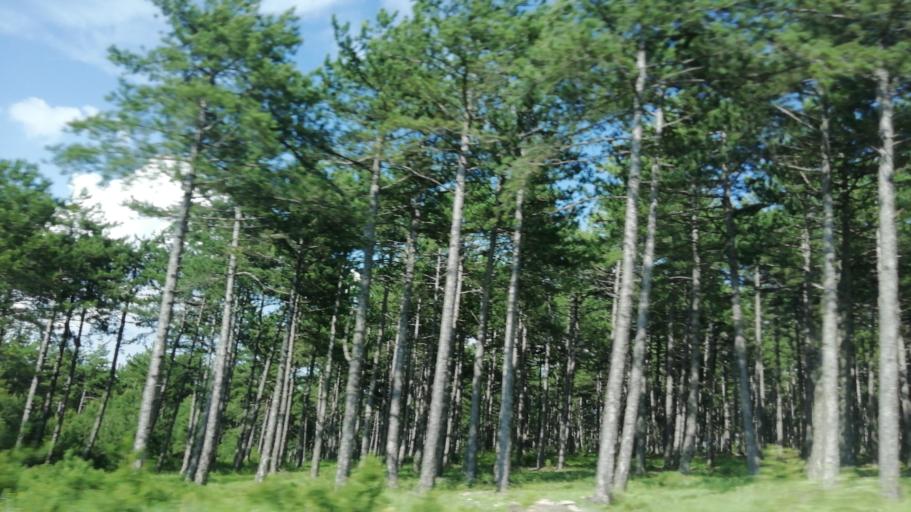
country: TR
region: Karabuk
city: Karabuk
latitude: 41.1159
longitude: 32.6052
